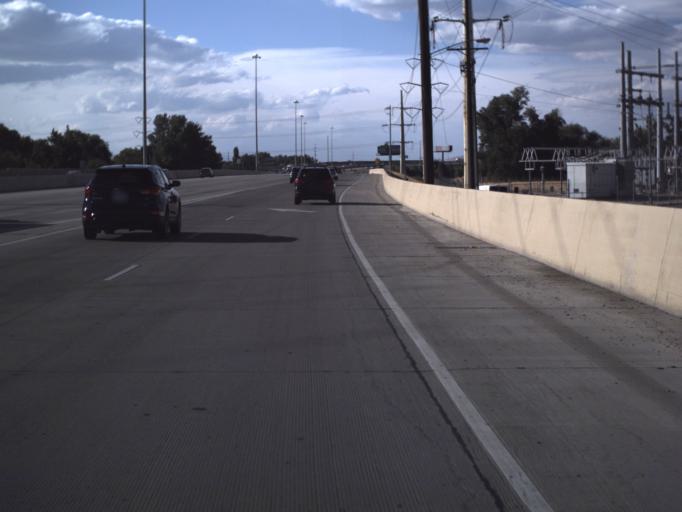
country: US
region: Utah
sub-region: Utah County
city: Provo
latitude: 40.2365
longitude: -111.6869
